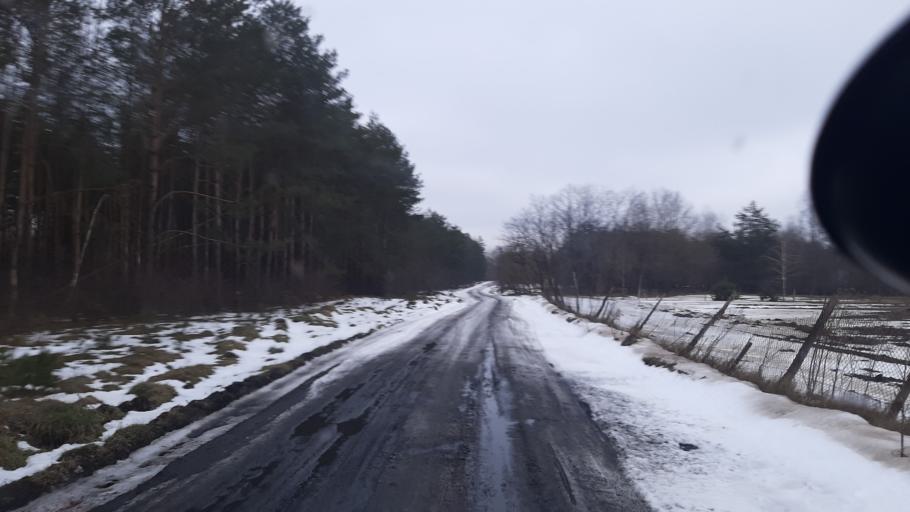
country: PL
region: Lublin Voivodeship
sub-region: Powiat wlodawski
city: Wlodawa
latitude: 51.5170
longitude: 23.5970
